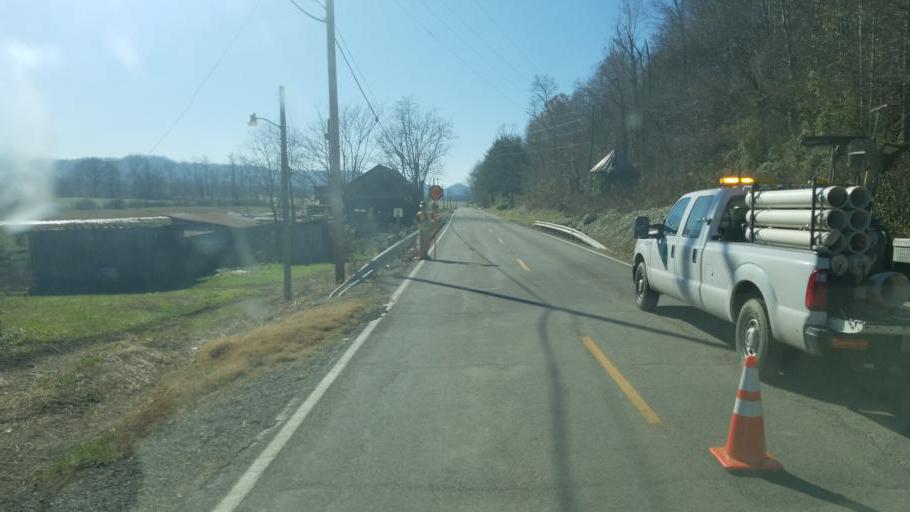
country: US
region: Ohio
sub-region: Scioto County
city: West Portsmouth
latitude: 38.6408
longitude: -83.1426
